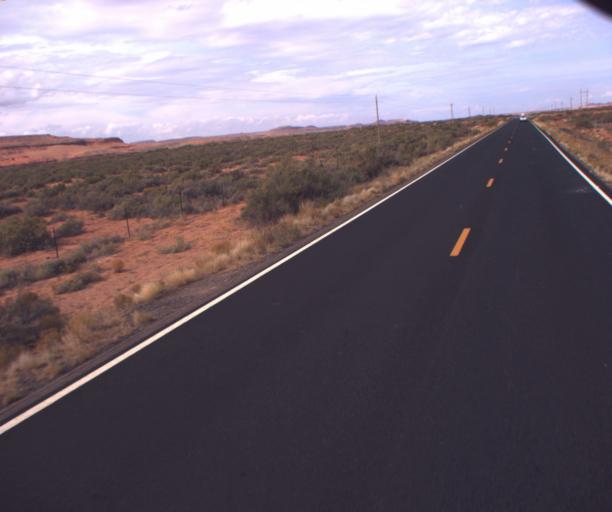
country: US
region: Arizona
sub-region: Apache County
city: Many Farms
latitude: 36.6232
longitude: -109.5824
